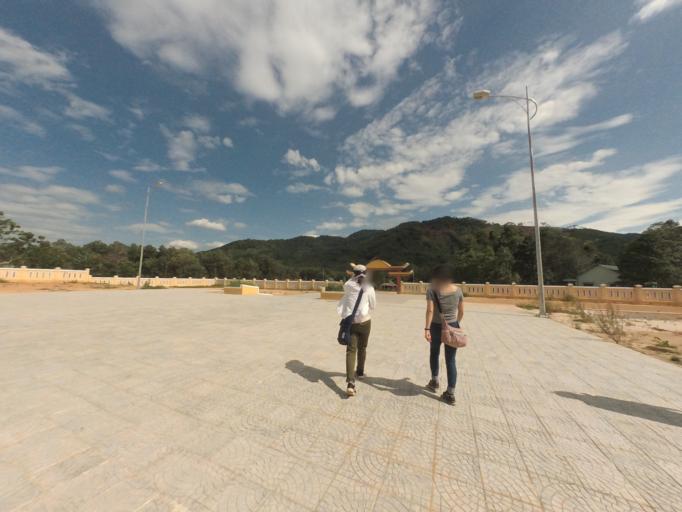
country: VN
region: Thua Thien-Hue
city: A Luoi
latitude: 16.3011
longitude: 107.3253
